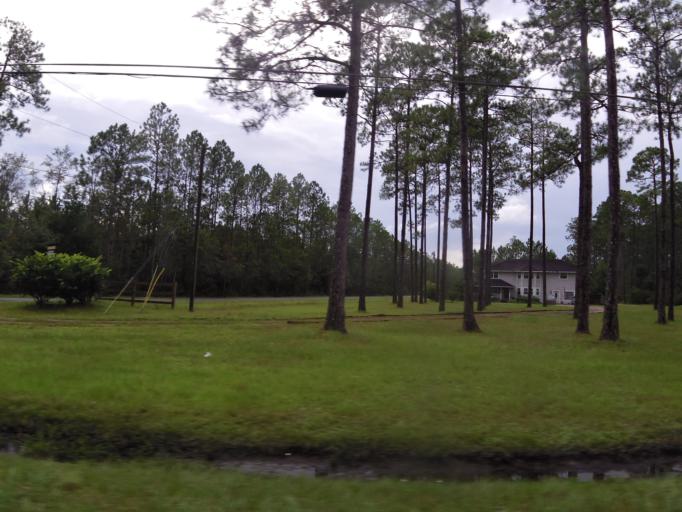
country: US
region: Florida
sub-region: Duval County
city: Baldwin
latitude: 30.3410
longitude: -81.9075
